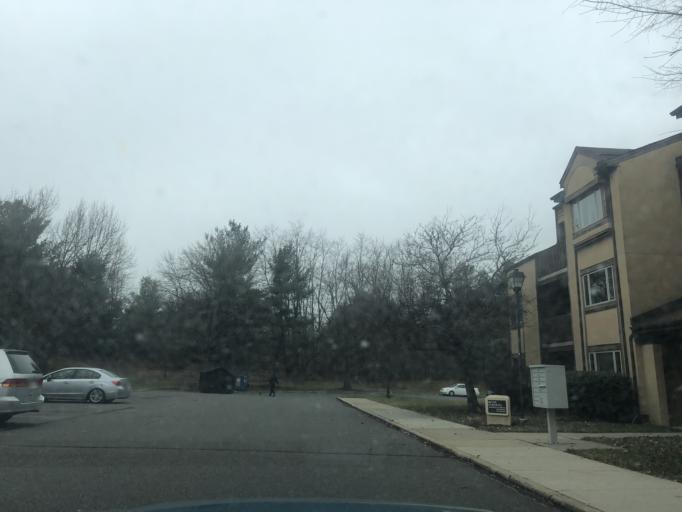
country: US
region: New Jersey
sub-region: Somerset County
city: Kingston
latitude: 40.3516
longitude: -74.6173
